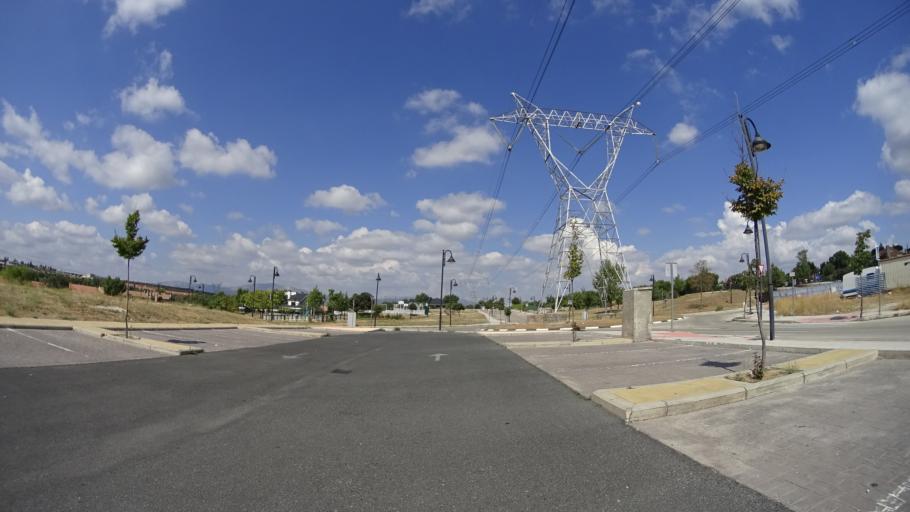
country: ES
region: Madrid
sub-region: Provincia de Madrid
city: Galapagar
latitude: 40.5846
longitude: -3.9972
